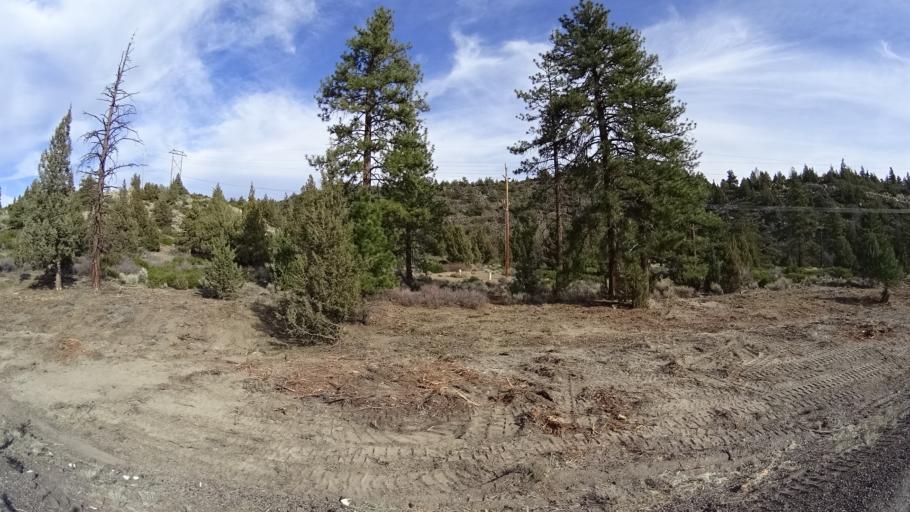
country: US
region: California
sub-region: Siskiyou County
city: Weed
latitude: 41.5143
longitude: -122.3651
